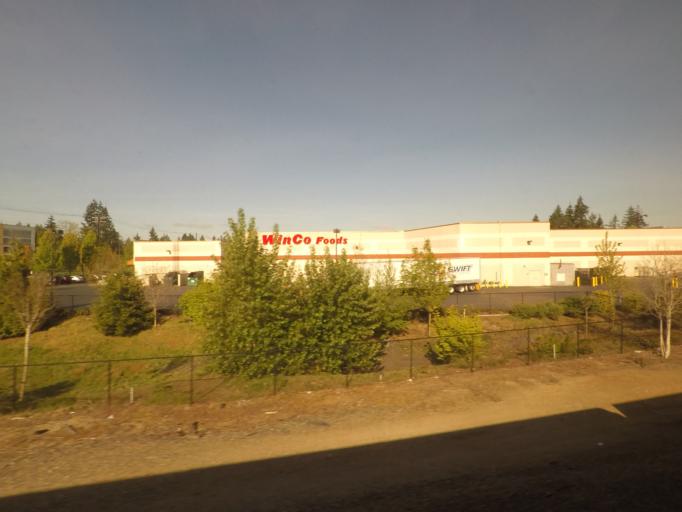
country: US
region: Washington
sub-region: Snohomish County
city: Marysville
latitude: 48.1006
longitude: -122.1759
